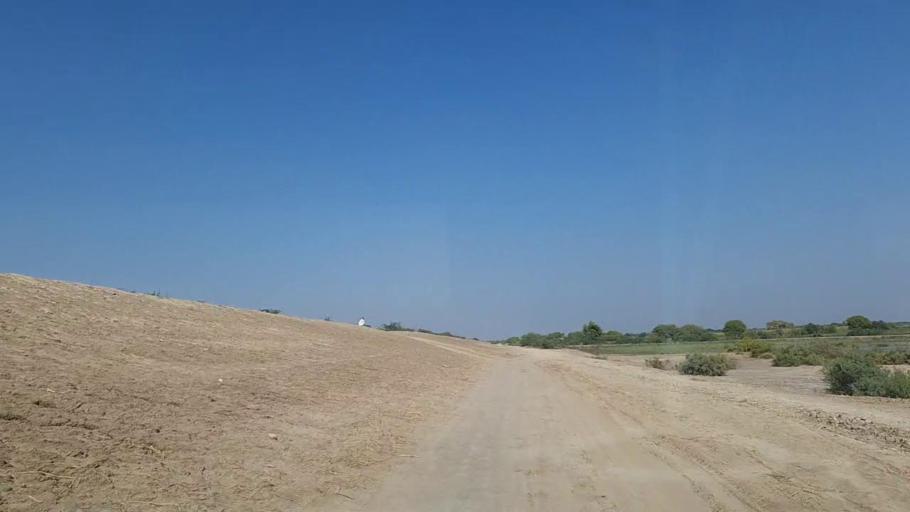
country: PK
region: Sindh
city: Chuhar Jamali
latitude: 24.4721
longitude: 68.0082
